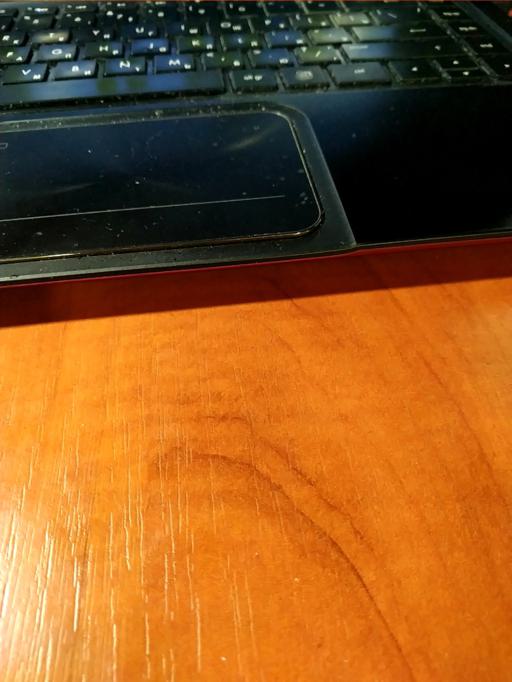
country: RU
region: Tverskaya
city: Zubtsov
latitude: 56.1602
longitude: 34.6044
